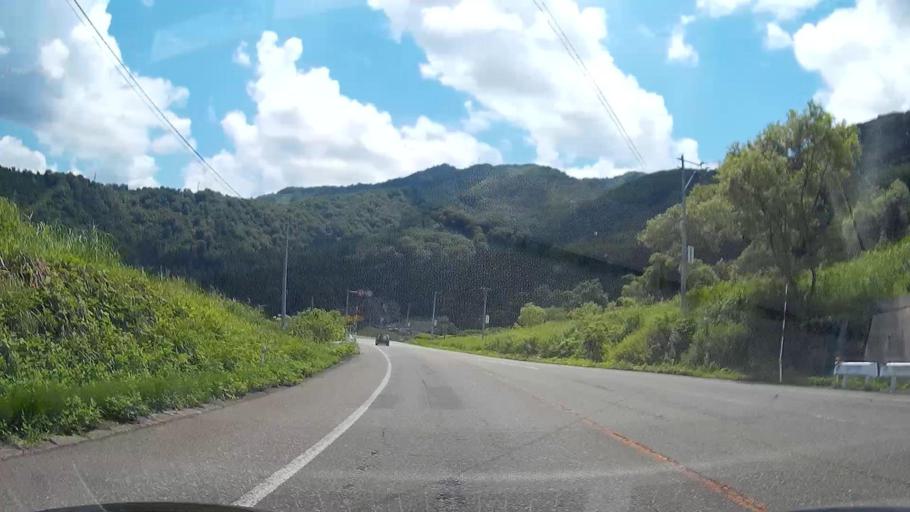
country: JP
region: Niigata
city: Shiozawa
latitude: 36.9113
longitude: 138.7961
